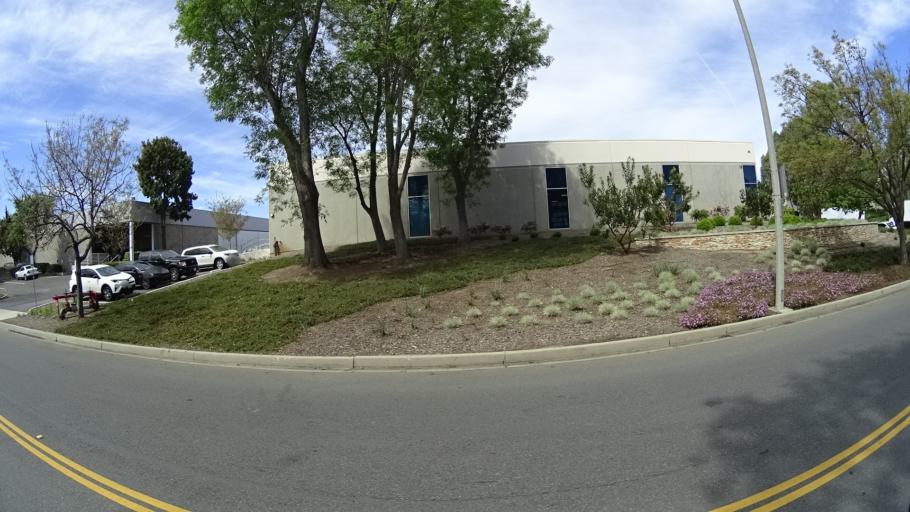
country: US
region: California
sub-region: Ventura County
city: Casa Conejo
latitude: 34.1923
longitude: -118.9299
